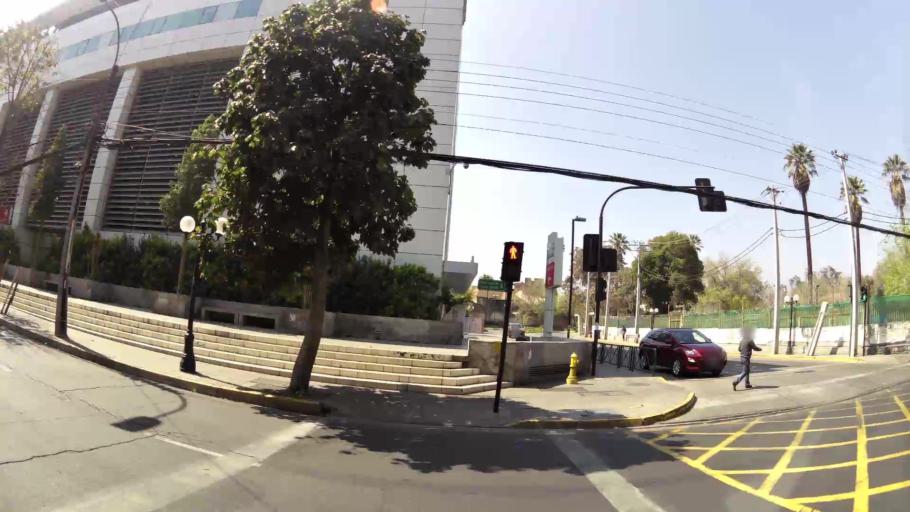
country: CL
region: Santiago Metropolitan
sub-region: Provincia de Santiago
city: Santiago
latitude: -33.4350
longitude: -70.6259
